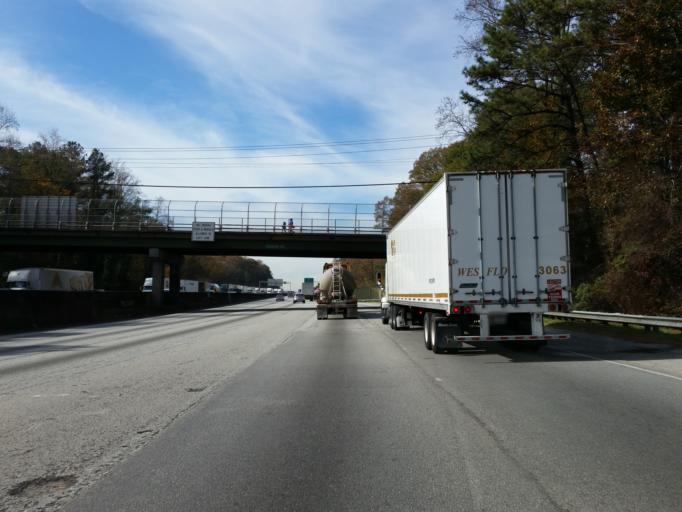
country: US
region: Georgia
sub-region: Cobb County
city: Mableton
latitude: 33.7665
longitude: -84.4994
